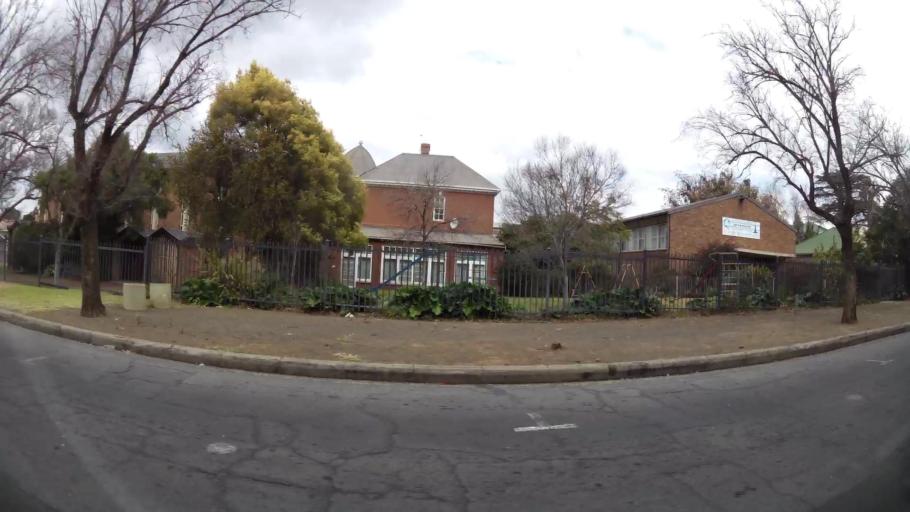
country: ZA
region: Orange Free State
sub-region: Mangaung Metropolitan Municipality
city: Bloemfontein
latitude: -29.1079
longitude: 26.2198
